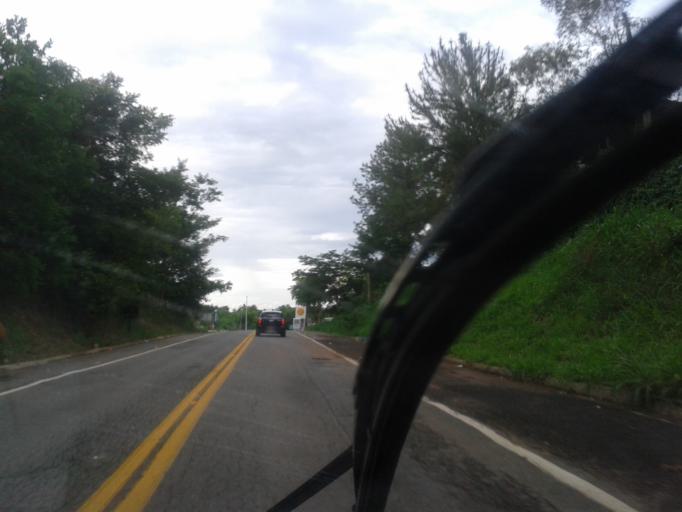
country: BR
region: Goias
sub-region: Caldas Novas
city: Caldas Novas
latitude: -17.7661
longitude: -48.7545
